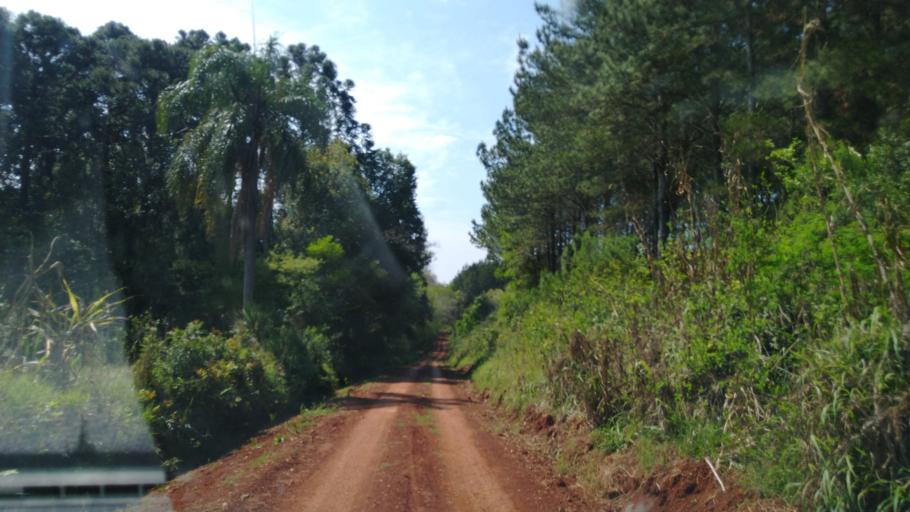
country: AR
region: Misiones
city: Capiovi
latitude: -26.9438
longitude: -55.0518
